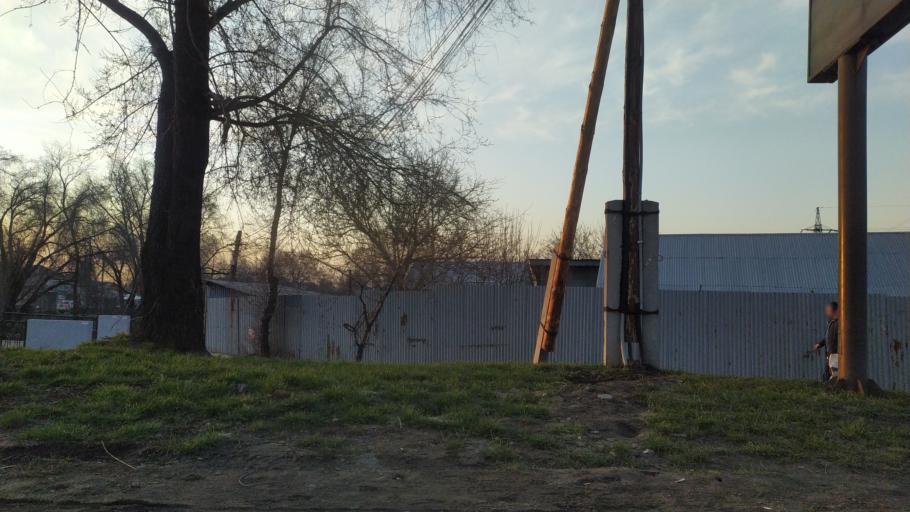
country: KZ
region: Almaty Qalasy
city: Almaty
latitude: 43.2217
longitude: 76.8829
